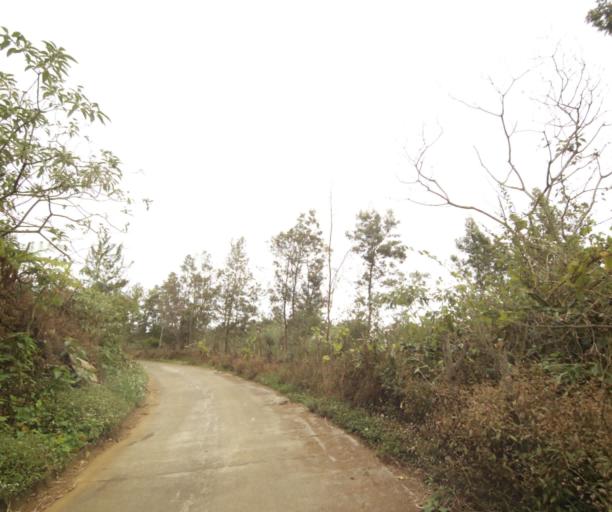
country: RE
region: Reunion
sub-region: Reunion
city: Saint-Paul
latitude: -21.0141
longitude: 55.3568
